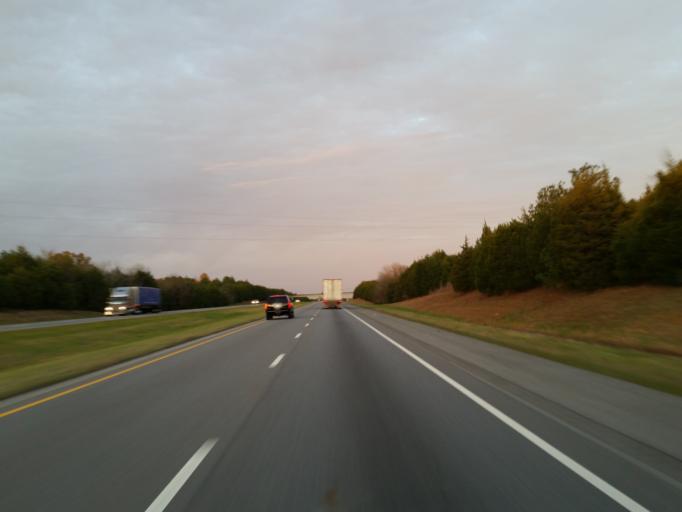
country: US
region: Alabama
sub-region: Sumter County
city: Livingston
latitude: 32.6749
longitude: -88.1688
